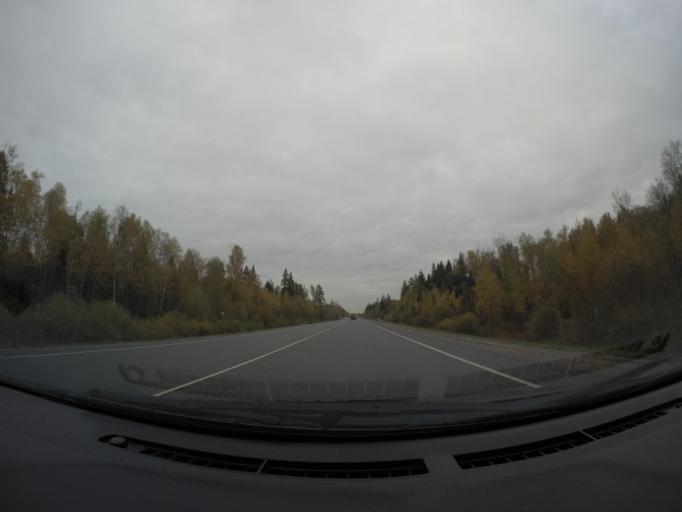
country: RU
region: Moskovskaya
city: Fryazevo
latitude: 55.7101
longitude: 38.4277
